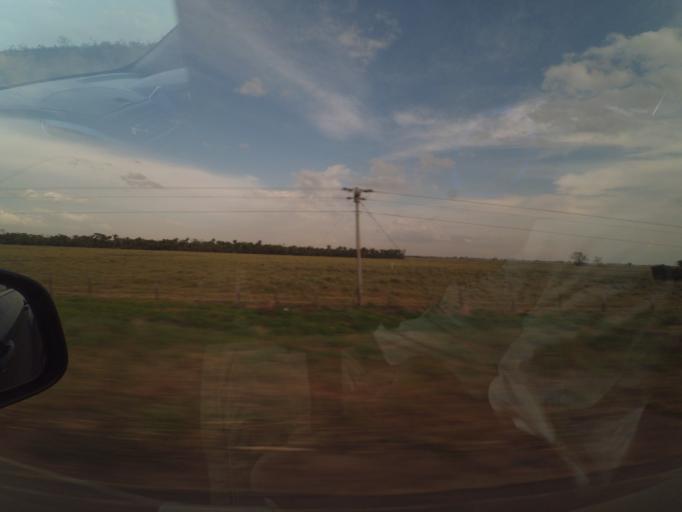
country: BO
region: Santa Cruz
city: Okinawa Numero Uno
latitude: -17.2355
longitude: -62.9560
